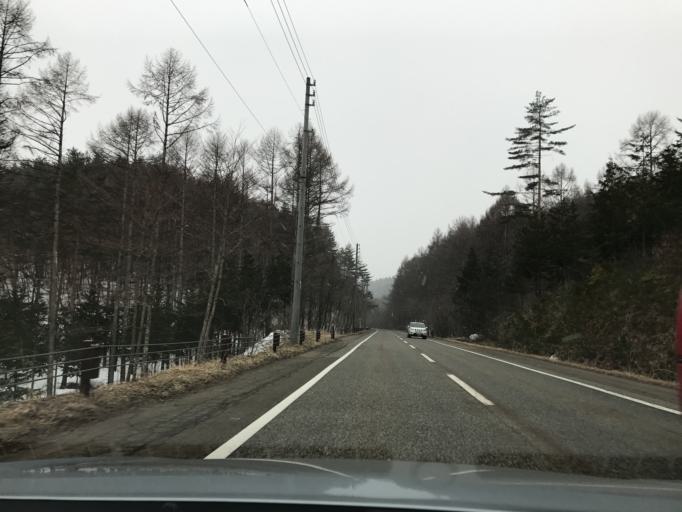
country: JP
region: Nagano
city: Omachi
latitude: 36.5482
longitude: 137.8632
